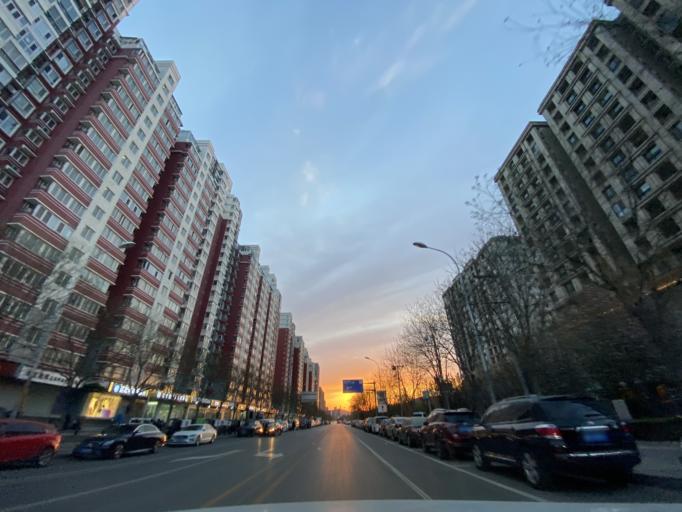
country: CN
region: Beijing
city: Qinghe
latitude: 40.0163
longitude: 116.3680
